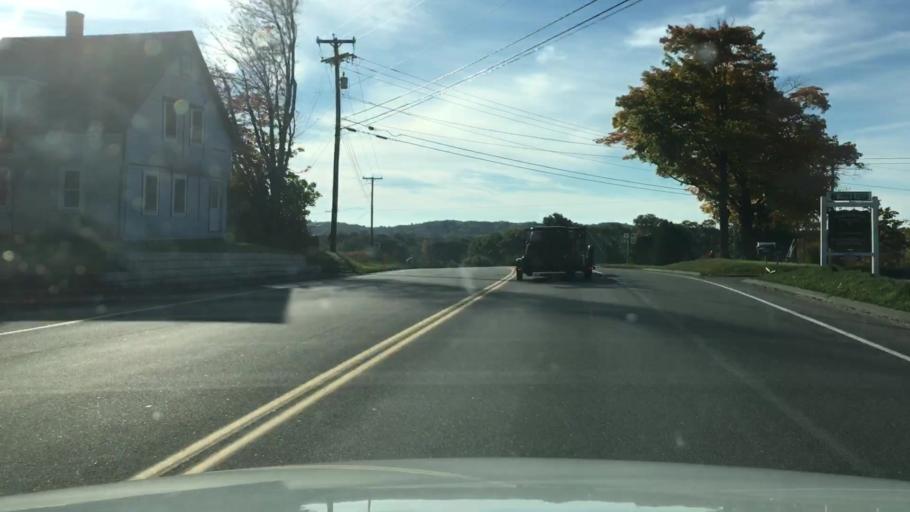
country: US
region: Maine
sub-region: Knox County
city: Warren
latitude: 44.0813
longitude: -69.2256
